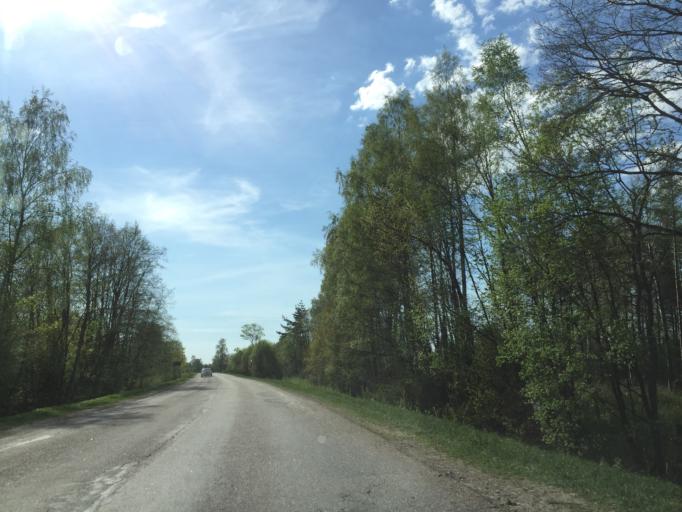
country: LV
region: Limbazu Rajons
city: Limbazi
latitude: 57.5127
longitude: 24.7586
